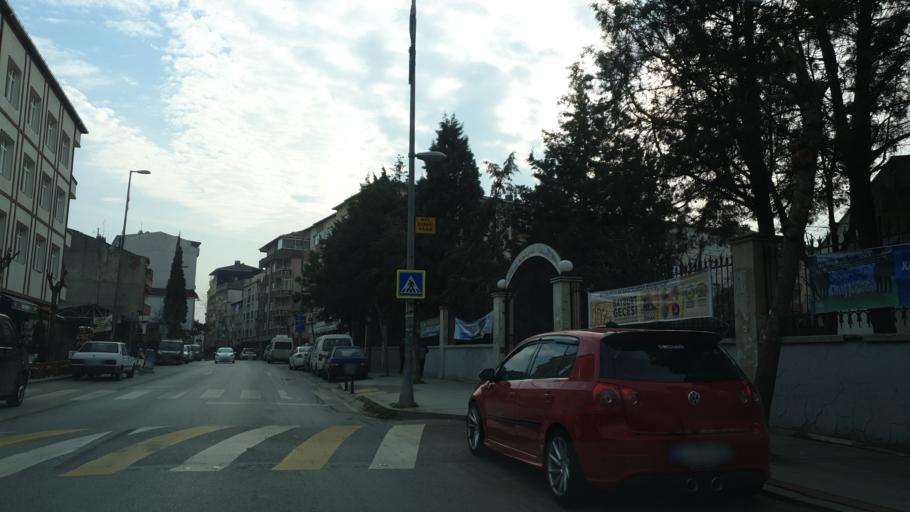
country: TR
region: Istanbul
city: Pendik
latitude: 40.8784
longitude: 29.2741
